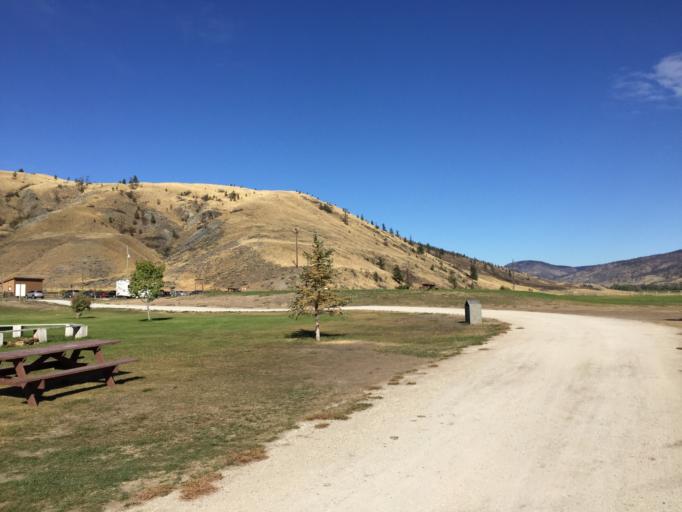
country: CA
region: British Columbia
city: Cache Creek
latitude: 50.8856
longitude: -121.4083
